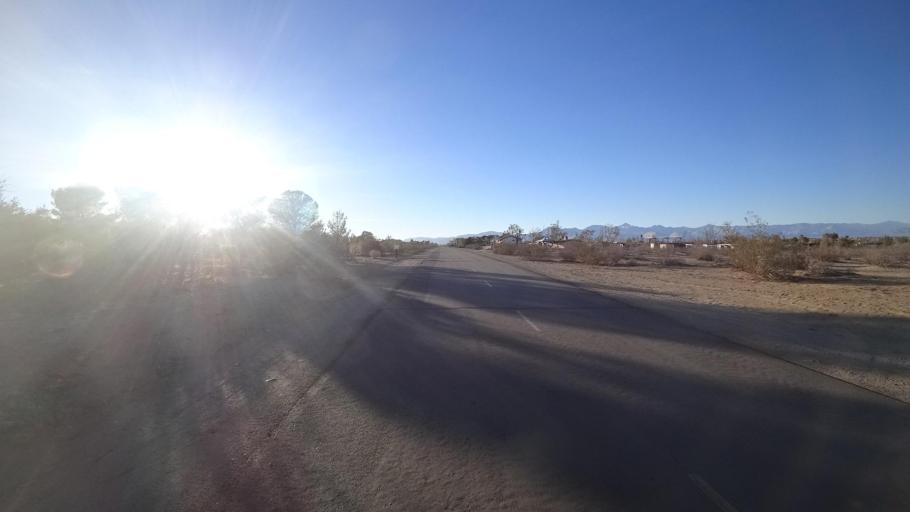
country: US
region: California
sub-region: Kern County
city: Ridgecrest
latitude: 35.5865
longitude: -117.6585
